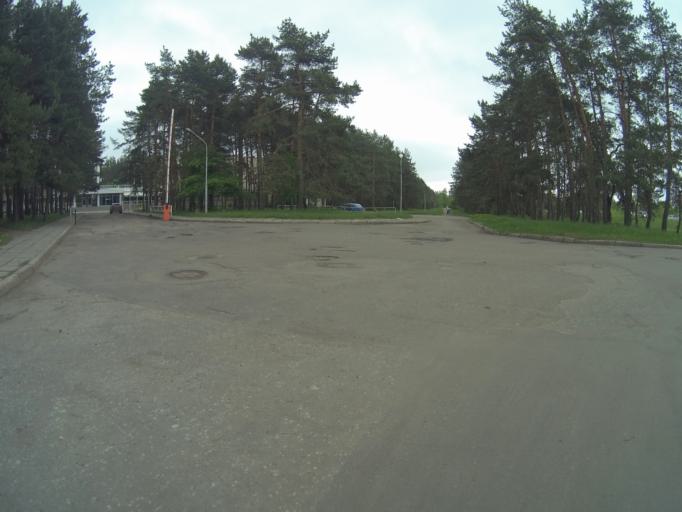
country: RU
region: Vladimir
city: Kommunar
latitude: 56.1059
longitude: 40.4351
